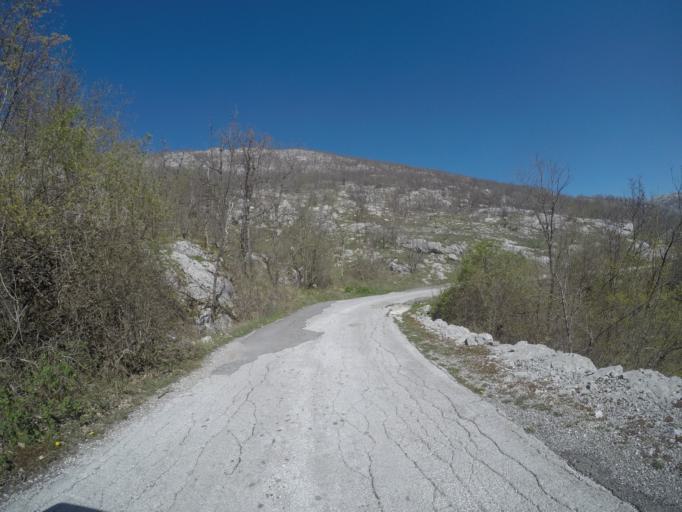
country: ME
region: Cetinje
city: Cetinje
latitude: 42.5351
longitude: 18.9786
